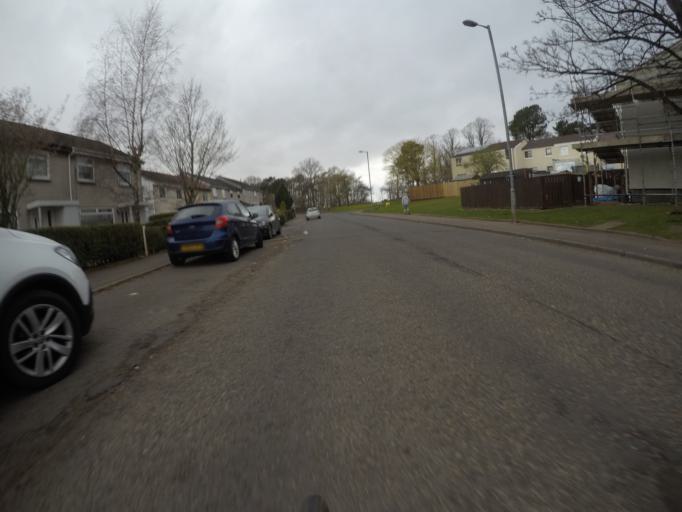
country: GB
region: Scotland
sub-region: East Ayrshire
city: Kilmarnock
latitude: 55.6188
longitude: -4.4792
